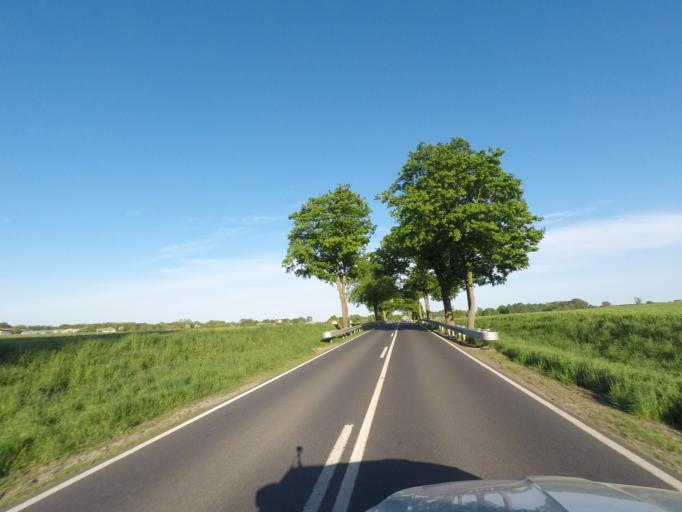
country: DE
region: Brandenburg
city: Hohenfinow
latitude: 52.8143
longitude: 13.9133
